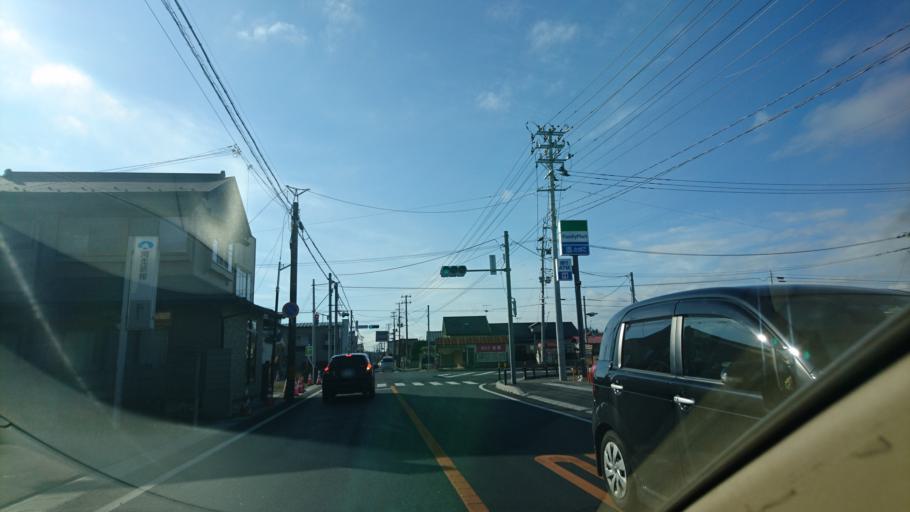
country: JP
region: Miyagi
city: Yamoto
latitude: 38.4715
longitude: 141.2108
